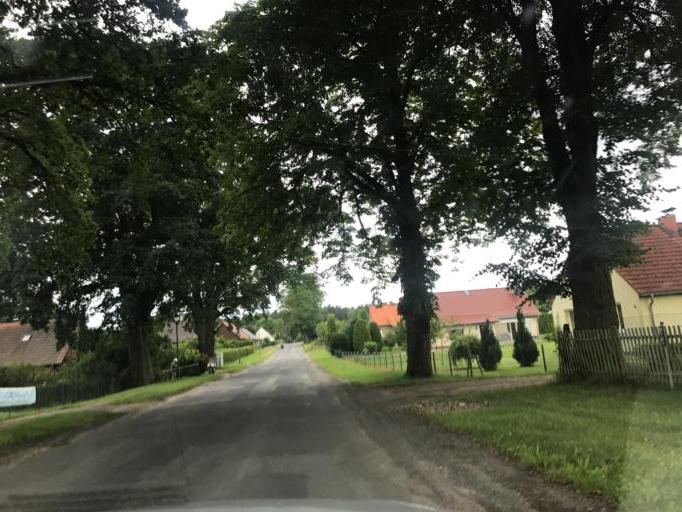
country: DE
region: Mecklenburg-Vorpommern
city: Rechlin
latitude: 53.2327
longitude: 12.7157
